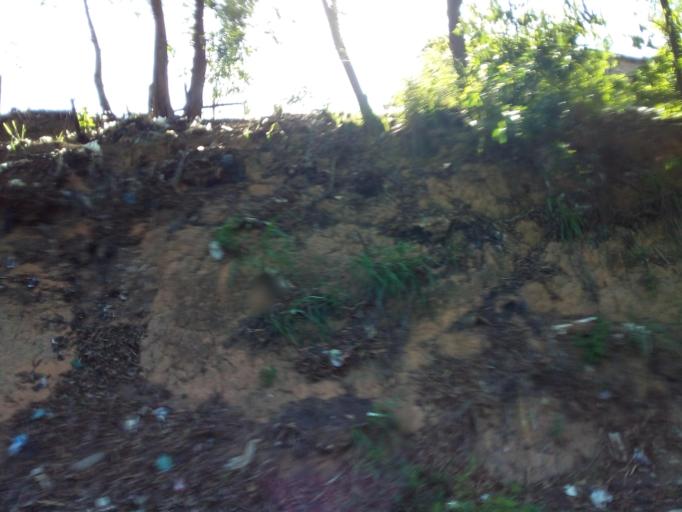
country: BR
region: Espirito Santo
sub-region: Vitoria
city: Vitoria
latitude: -20.2967
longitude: -40.3754
